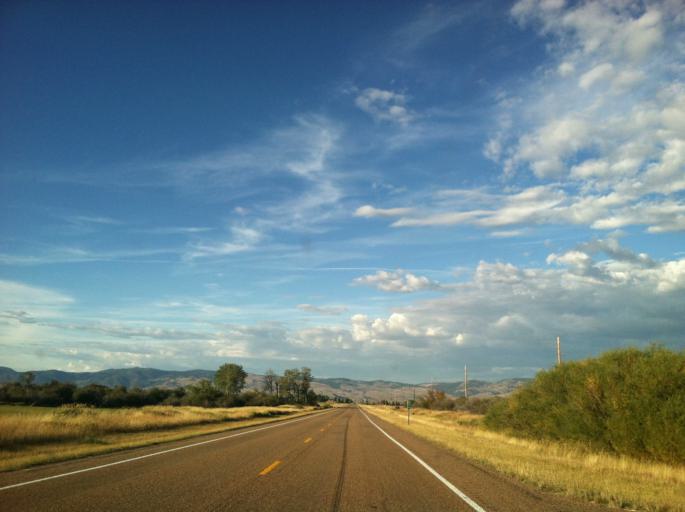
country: US
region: Montana
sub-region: Granite County
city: Philipsburg
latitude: 46.5669
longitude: -113.2091
